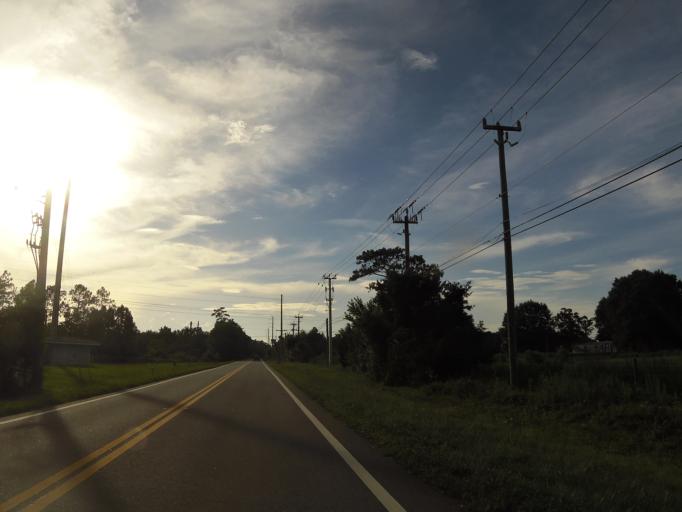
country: US
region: Florida
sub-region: Clay County
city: Green Cove Springs
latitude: 29.9885
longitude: -81.5300
